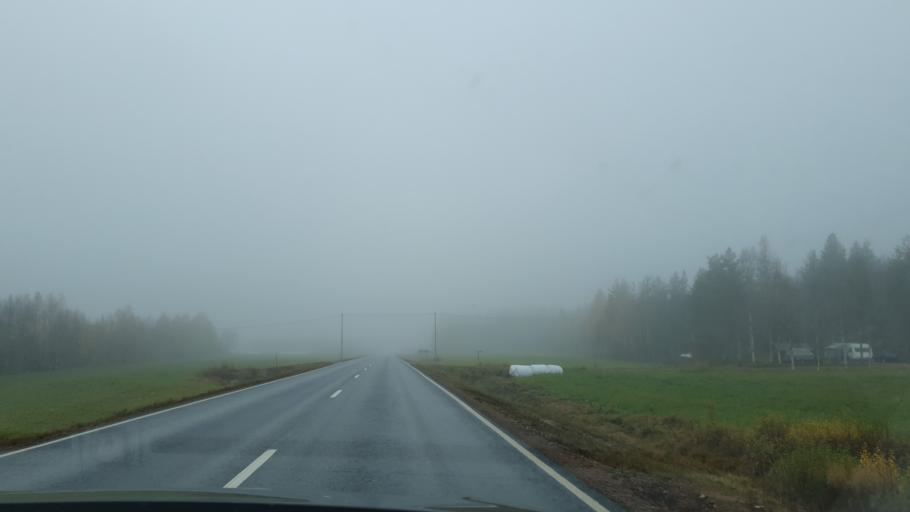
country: FI
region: Lapland
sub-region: Rovaniemi
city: Rovaniemi
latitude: 66.8027
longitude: 25.4134
